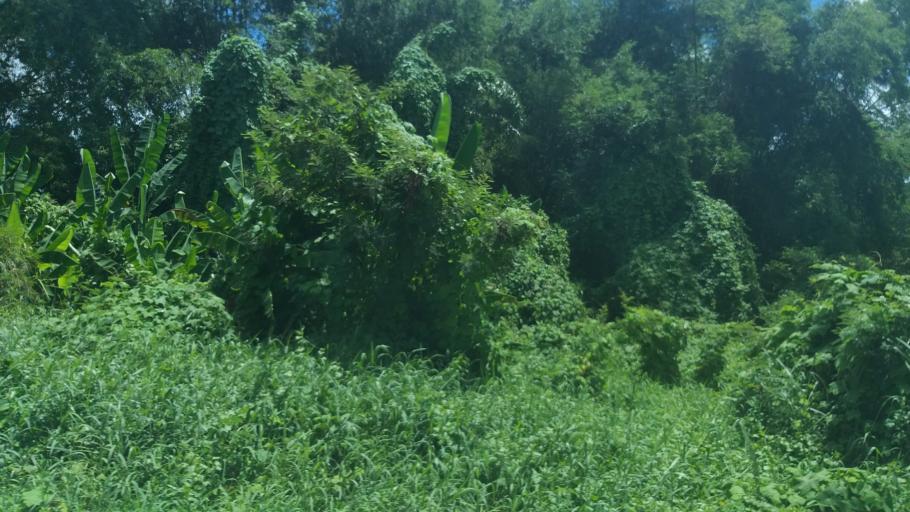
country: TH
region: Nakhon Nayok
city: Ban Na
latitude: 14.2798
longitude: 101.0665
